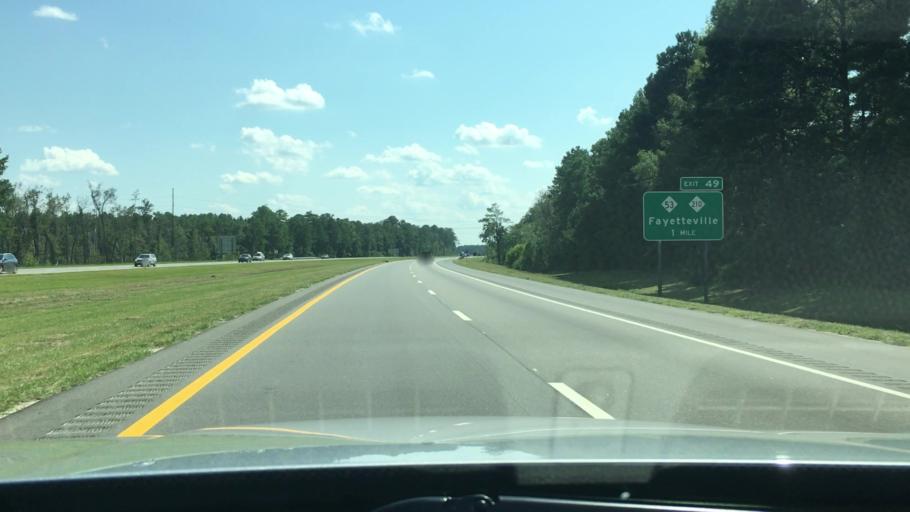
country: US
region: North Carolina
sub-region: Cumberland County
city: Vander
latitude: 35.0231
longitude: -78.8100
